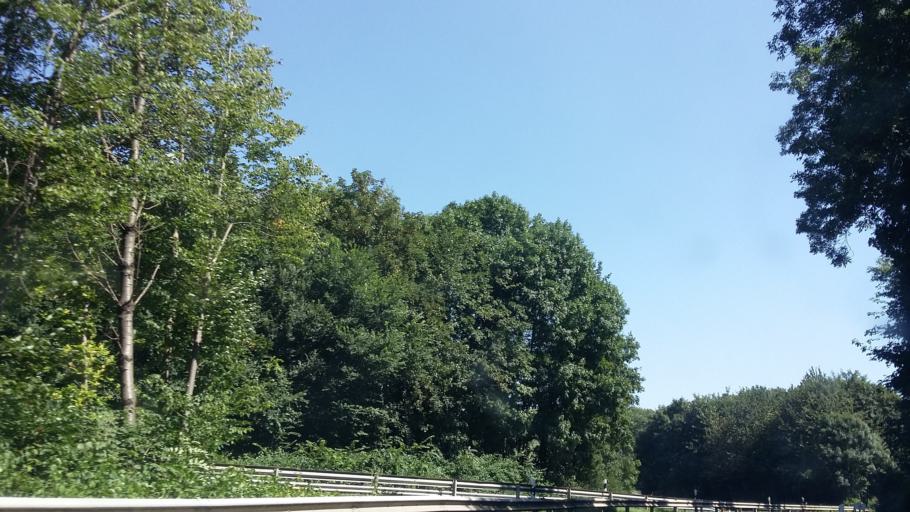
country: DE
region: Bavaria
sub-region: Swabia
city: Augsburg
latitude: 48.4080
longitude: 10.9207
